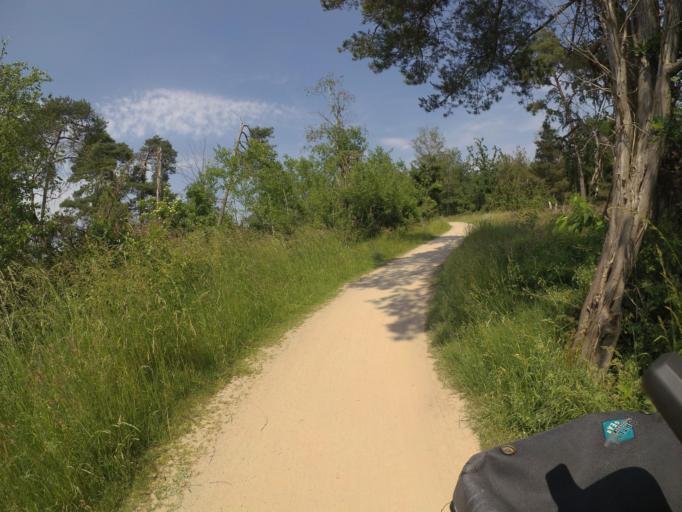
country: NL
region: Overijssel
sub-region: Gemeente Hof van Twente
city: Markelo
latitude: 52.3482
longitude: 6.4481
